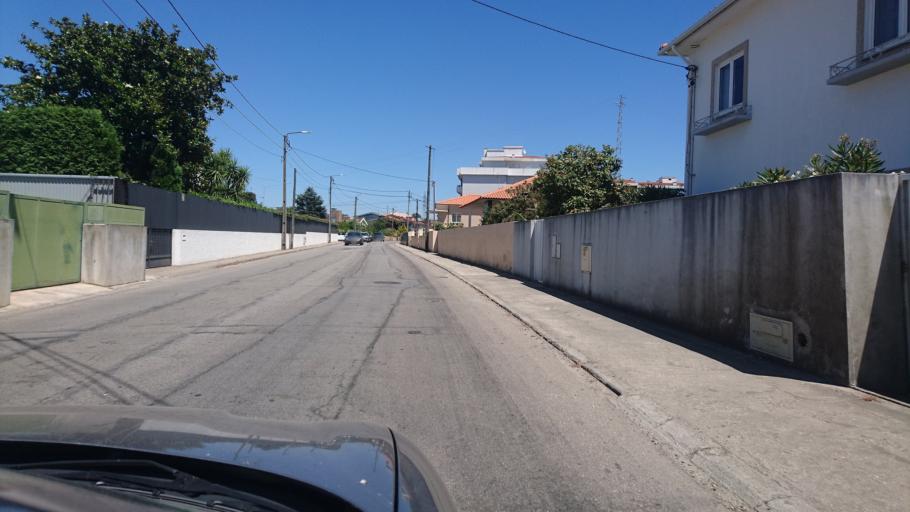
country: PT
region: Aveiro
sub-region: Espinho
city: Souto
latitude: 40.9840
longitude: -8.6028
